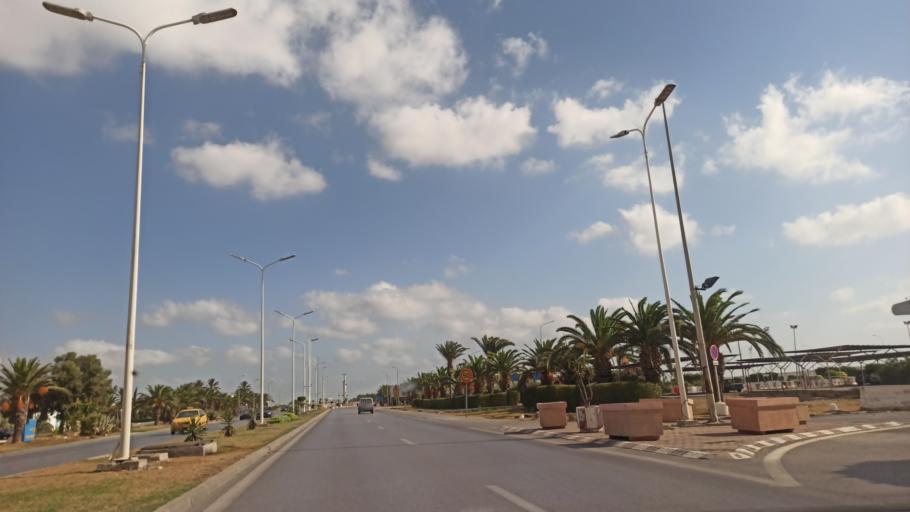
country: TN
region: Ariana
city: Ariana
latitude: 36.8380
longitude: 10.2136
